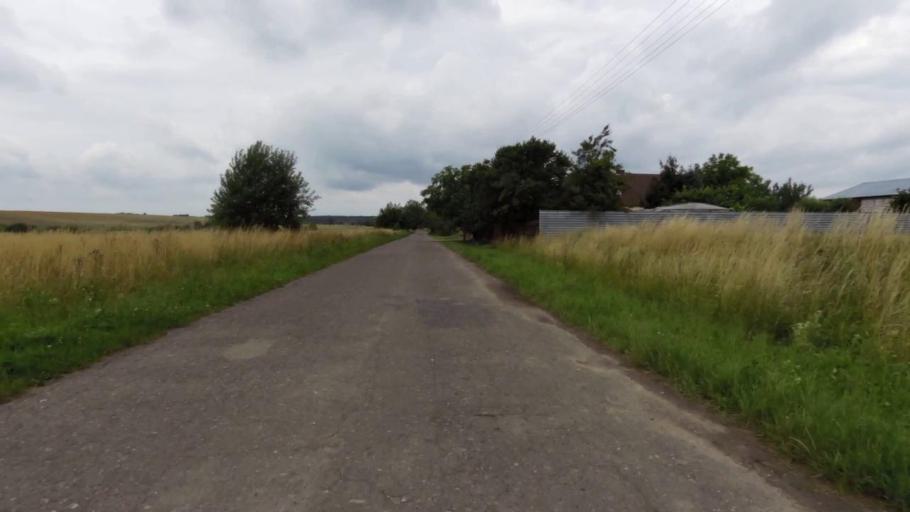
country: PL
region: West Pomeranian Voivodeship
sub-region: Powiat pyrzycki
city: Lipiany
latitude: 52.9662
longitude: 14.9486
